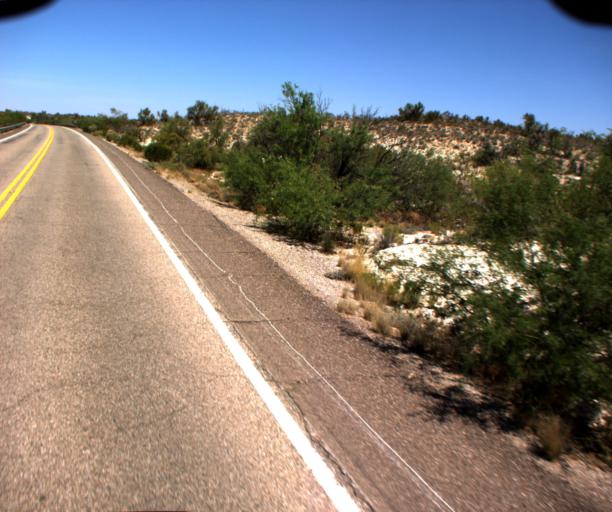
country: US
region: Arizona
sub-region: Gila County
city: Peridot
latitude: 33.2526
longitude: -110.2782
